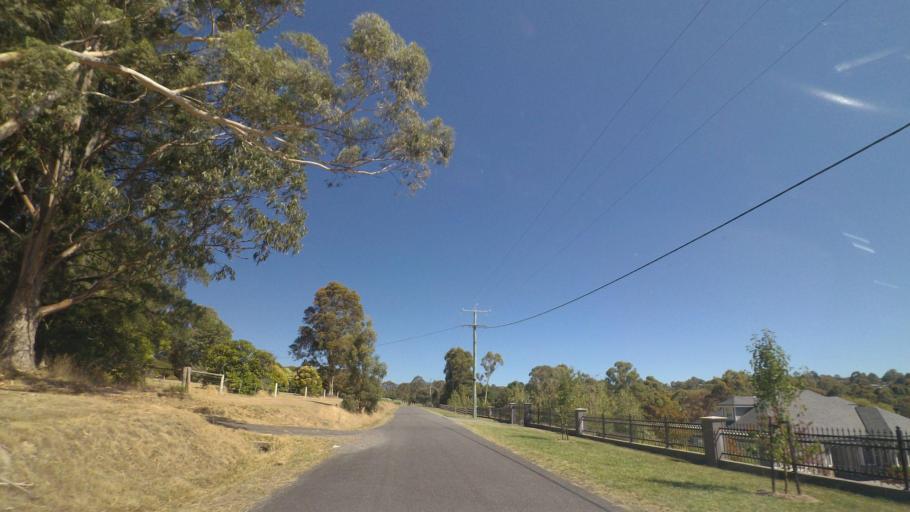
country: AU
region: Victoria
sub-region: Yarra Ranges
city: Chirnside Park
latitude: -37.7408
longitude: 145.3330
